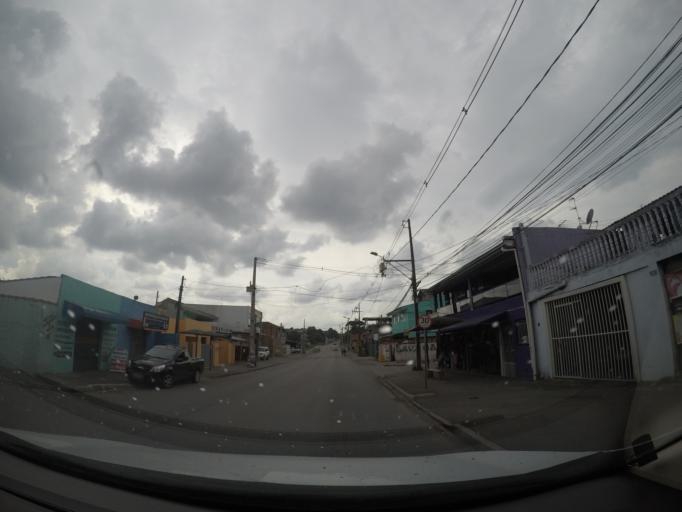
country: BR
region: Parana
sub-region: Sao Jose Dos Pinhais
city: Sao Jose dos Pinhais
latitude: -25.5492
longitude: -49.2468
